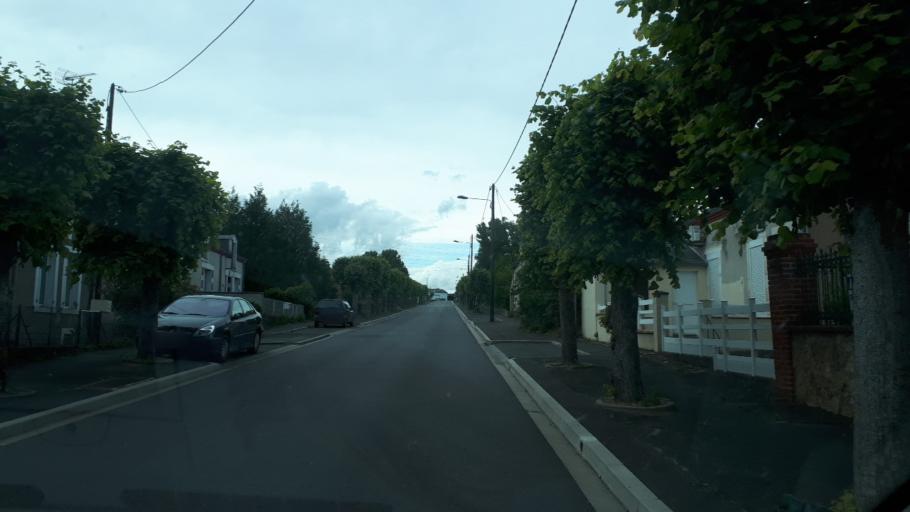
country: FR
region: Centre
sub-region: Departement de l'Indre
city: Reuilly
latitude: 47.0871
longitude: 2.0377
